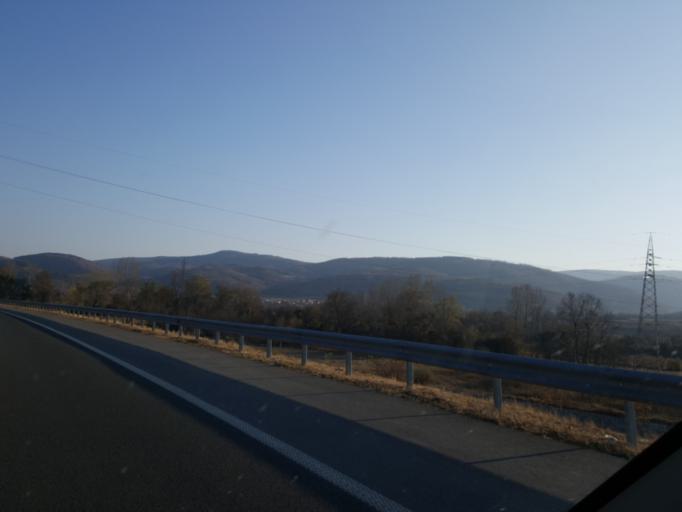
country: RS
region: Central Serbia
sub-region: Pirotski Okrug
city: Dimitrovgrad
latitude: 43.0254
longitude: 22.7249
